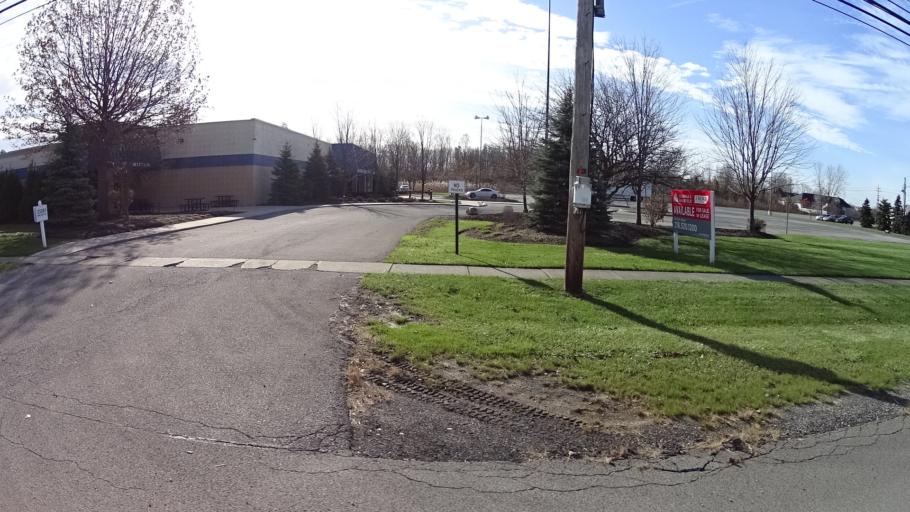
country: US
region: Ohio
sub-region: Lorain County
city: Avon Lake
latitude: 41.4933
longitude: -82.0450
